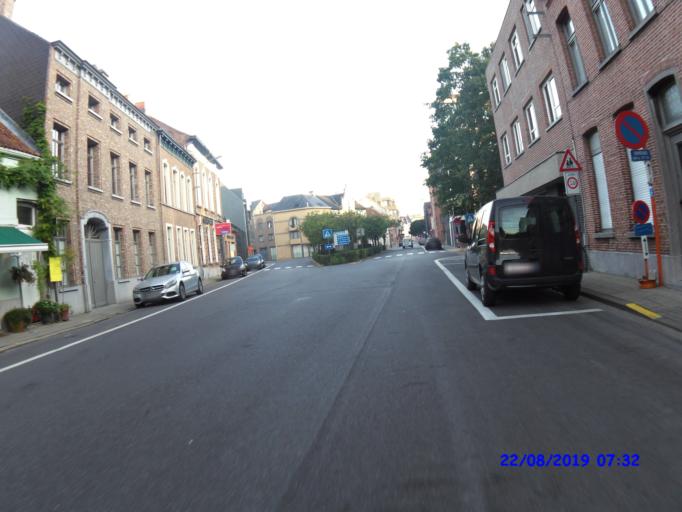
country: BE
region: Flanders
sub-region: Provincie Oost-Vlaanderen
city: Beveren
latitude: 51.2107
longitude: 4.2576
